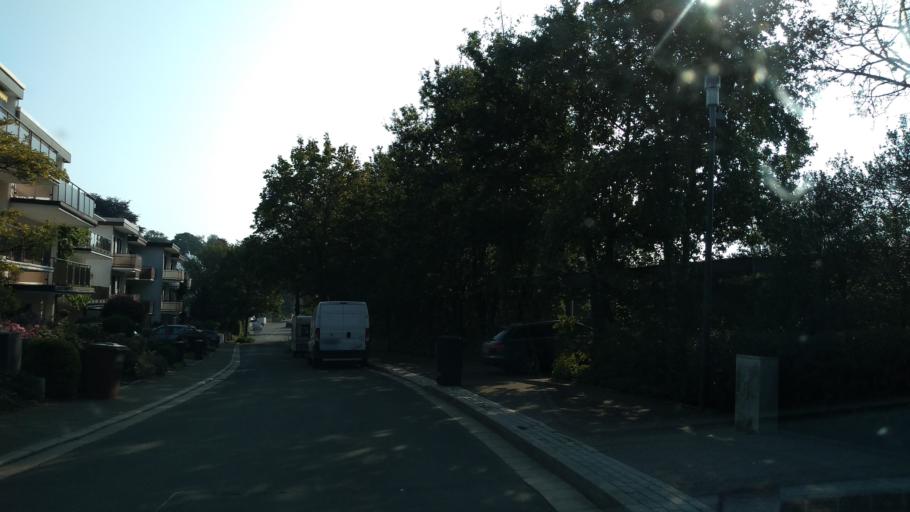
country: DE
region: North Rhine-Westphalia
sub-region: Regierungsbezirk Arnsberg
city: Luedenscheid
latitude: 51.2124
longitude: 7.5999
